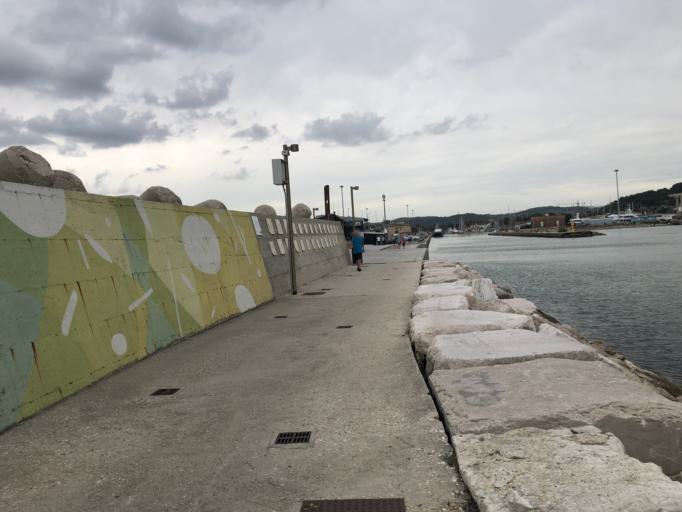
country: IT
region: The Marches
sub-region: Provincia di Pesaro e Urbino
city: Pesaro
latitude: 43.9260
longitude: 12.9070
